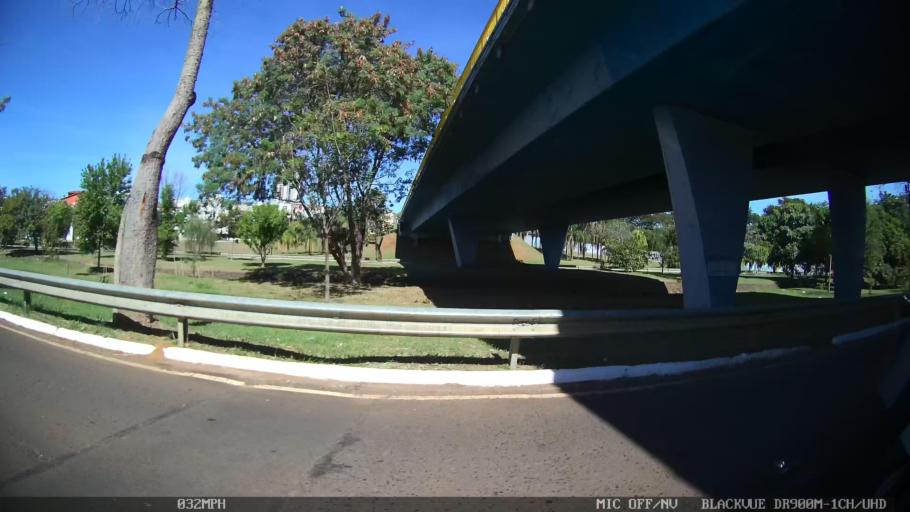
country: BR
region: Sao Paulo
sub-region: Franca
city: Franca
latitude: -20.5523
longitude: -47.4075
